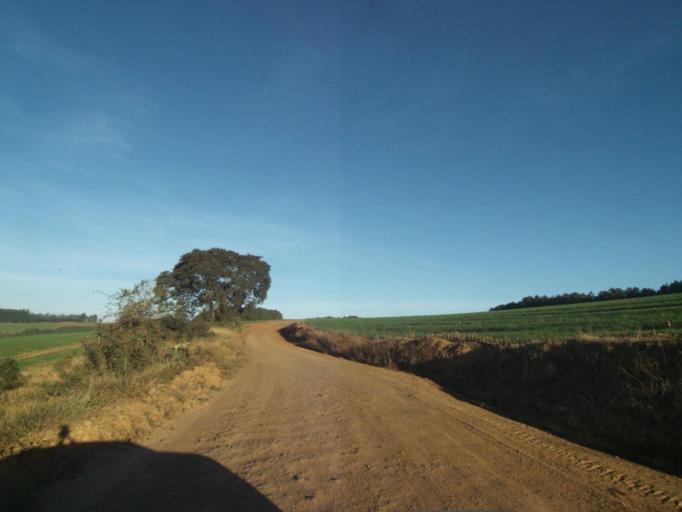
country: BR
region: Parana
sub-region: Telemaco Borba
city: Telemaco Borba
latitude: -24.4625
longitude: -50.5976
